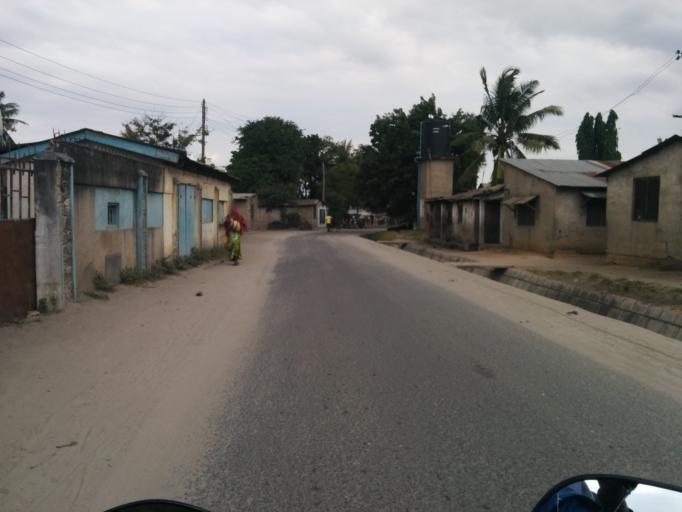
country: TZ
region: Dar es Salaam
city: Dar es Salaam
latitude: -6.8671
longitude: 39.2499
